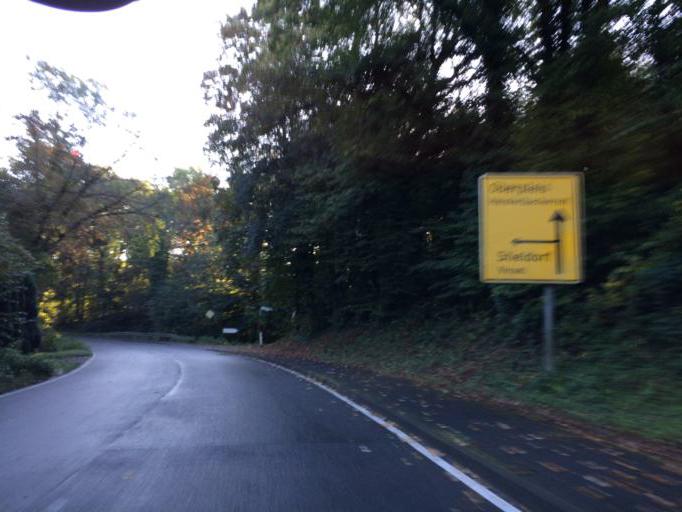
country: DE
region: North Rhine-Westphalia
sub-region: Regierungsbezirk Koln
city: Konigswinter
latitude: 50.6983
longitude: 7.2053
